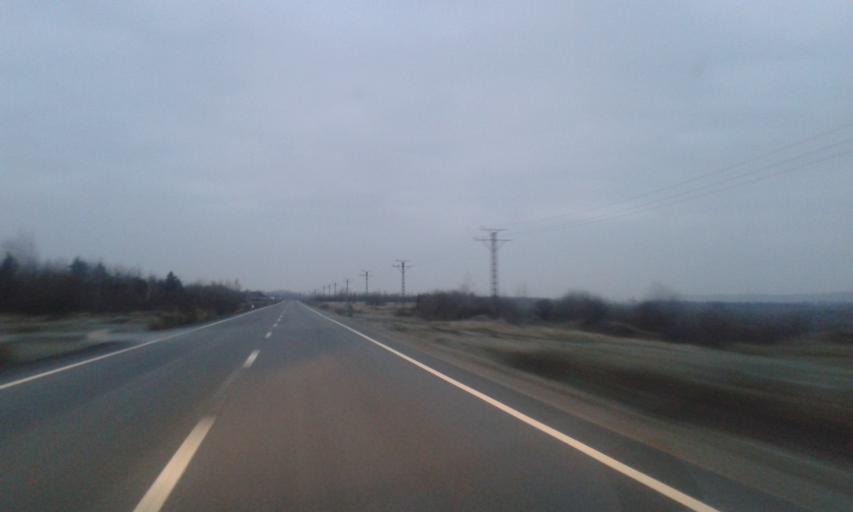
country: RO
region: Gorj
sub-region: Comuna Bumbesti-Jiu
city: Bumbesti-Jiu
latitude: 45.1459
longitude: 23.3704
